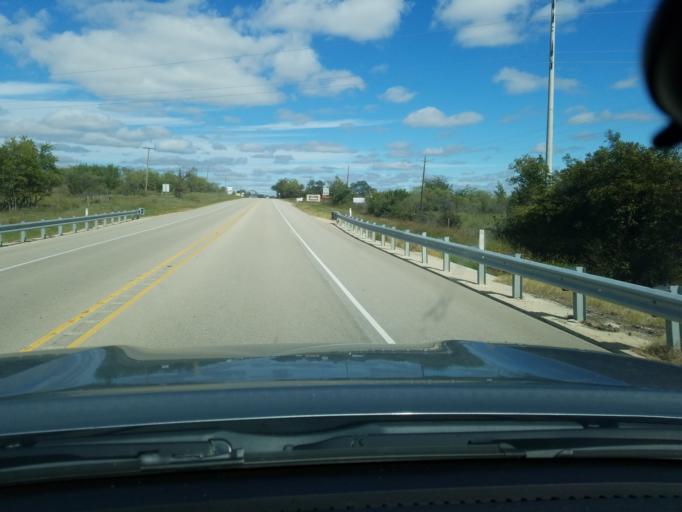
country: US
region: Texas
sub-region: Hamilton County
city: Hamilton
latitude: 31.6859
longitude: -98.1313
